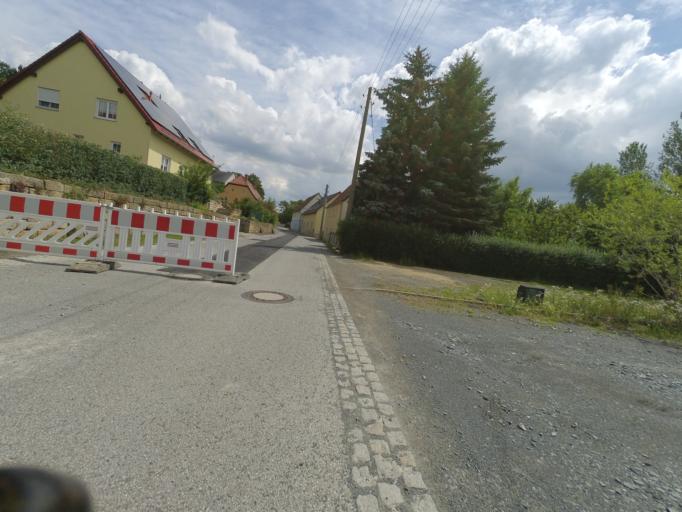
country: DE
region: Saxony
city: Heidenau
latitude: 50.9680
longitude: 13.8997
